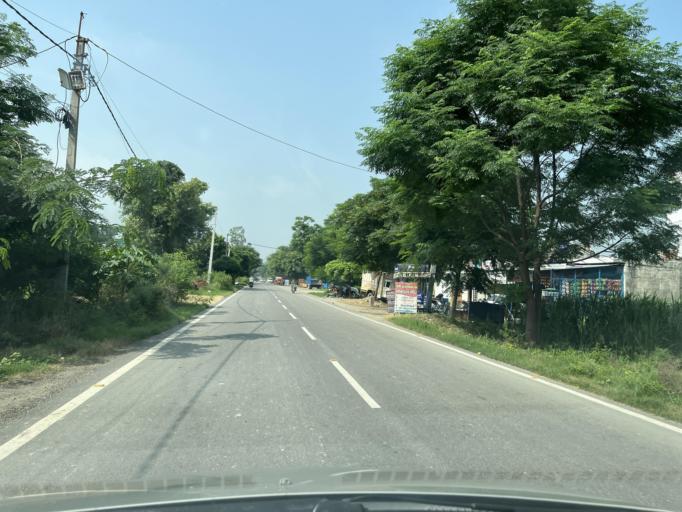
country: IN
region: Uttarakhand
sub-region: Udham Singh Nagar
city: Bazpur
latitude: 29.1826
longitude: 79.1809
